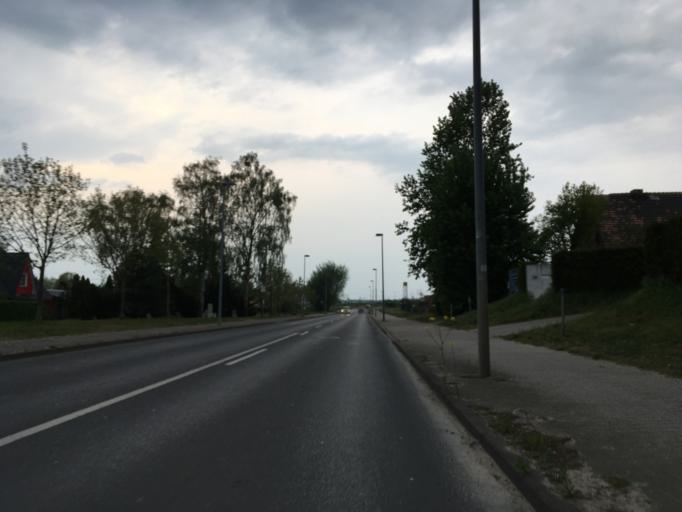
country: DE
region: Berlin
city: Wartenberg
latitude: 52.6056
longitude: 13.5235
